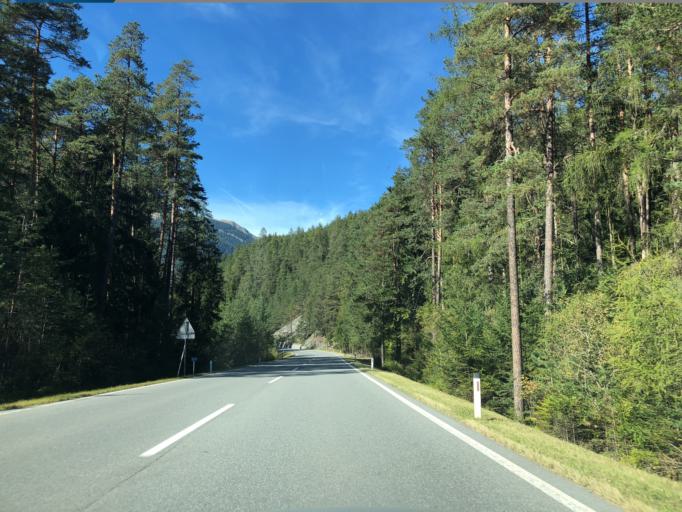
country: AT
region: Tyrol
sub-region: Politischer Bezirk Imst
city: Umhausen
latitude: 47.1239
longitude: 10.9292
